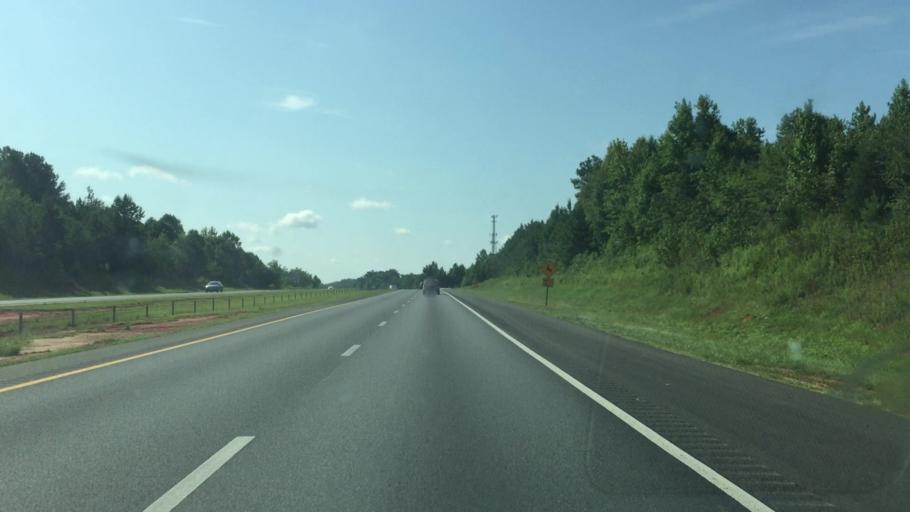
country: US
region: North Carolina
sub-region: Mecklenburg County
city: Mint Hill
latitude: 35.2170
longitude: -80.6475
